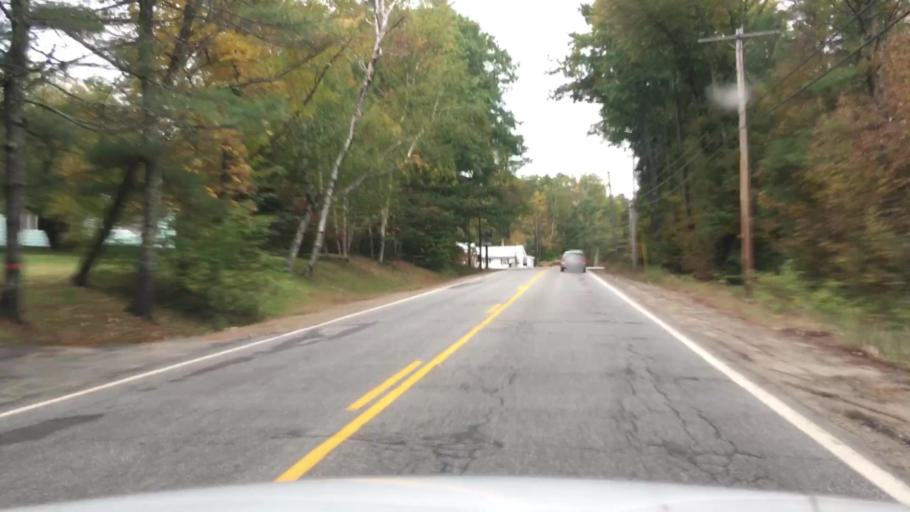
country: US
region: Maine
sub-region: Oxford County
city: Norway
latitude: 44.2163
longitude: -70.5825
